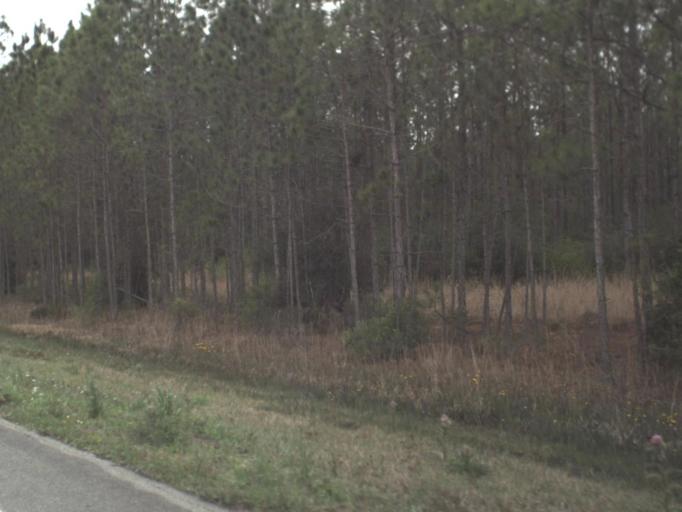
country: US
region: Florida
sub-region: Gulf County
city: Port Saint Joe
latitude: 29.9053
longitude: -85.2080
